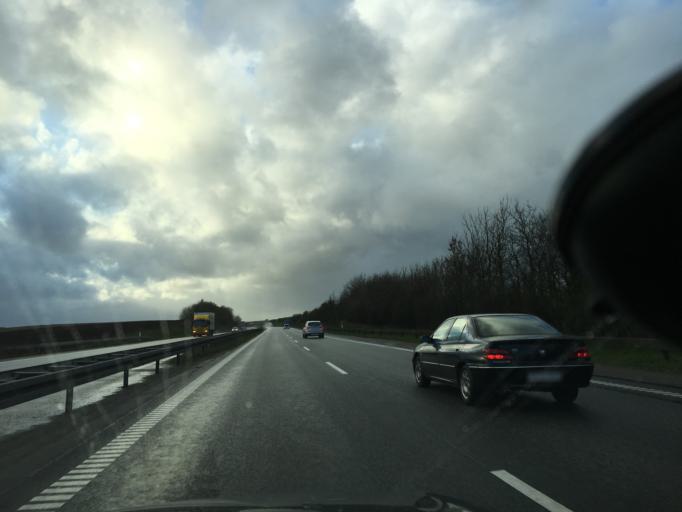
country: DK
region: North Denmark
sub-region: Mariagerfjord Kommune
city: Hobro
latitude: 56.5947
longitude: 9.7646
